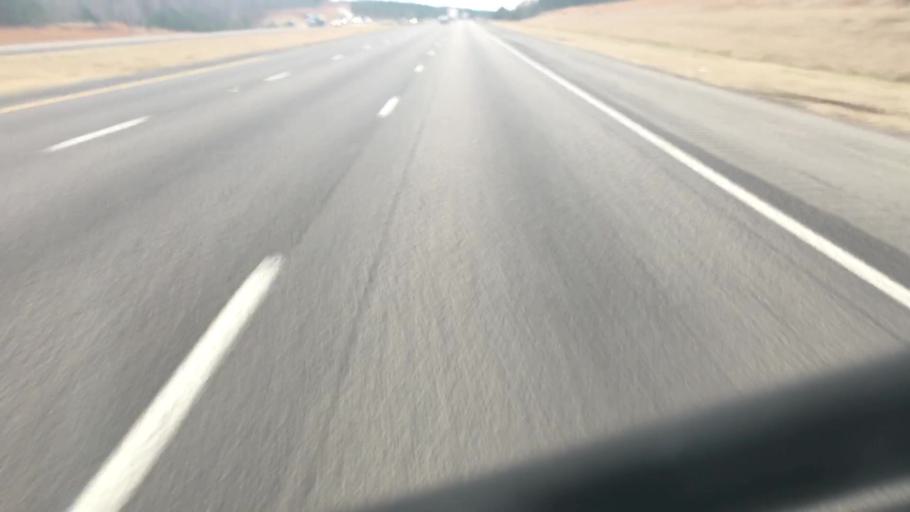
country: US
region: Alabama
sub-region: Walker County
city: Dora
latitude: 33.6654
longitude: -87.0584
